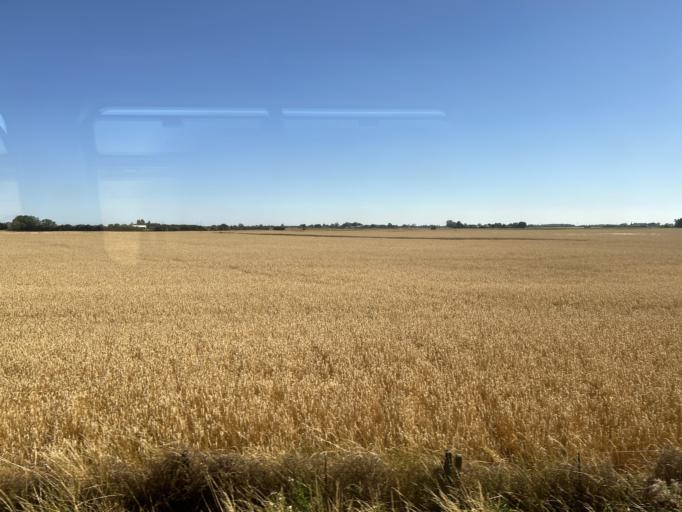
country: GB
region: England
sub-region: Lincolnshire
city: Spilsby
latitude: 53.1308
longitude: 0.1500
